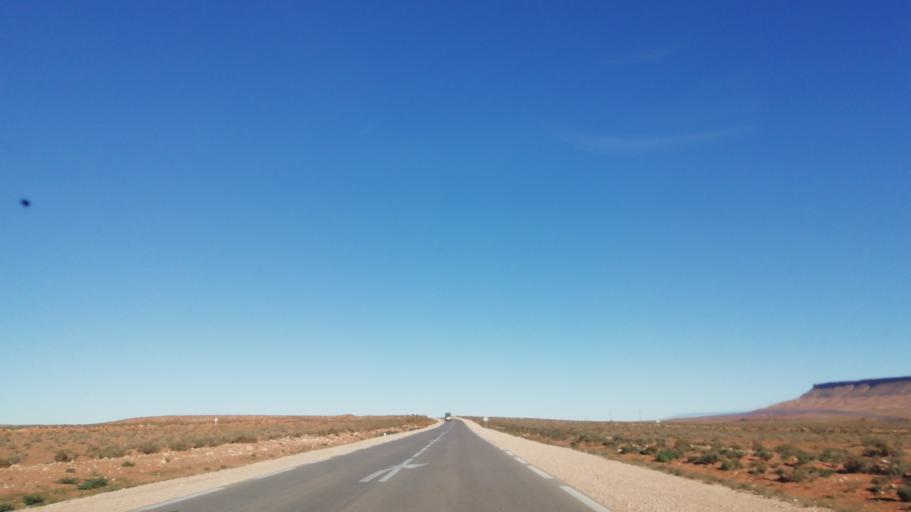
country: DZ
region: El Bayadh
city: El Abiodh Sidi Cheikh
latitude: 33.0931
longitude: 0.1973
